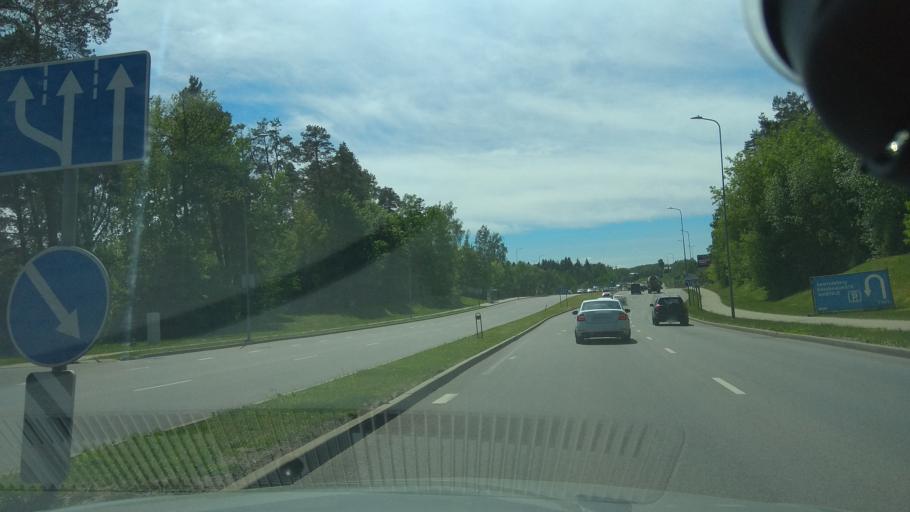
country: LT
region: Vilnius County
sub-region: Vilnius
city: Fabijoniskes
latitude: 54.7551
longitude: 25.2707
